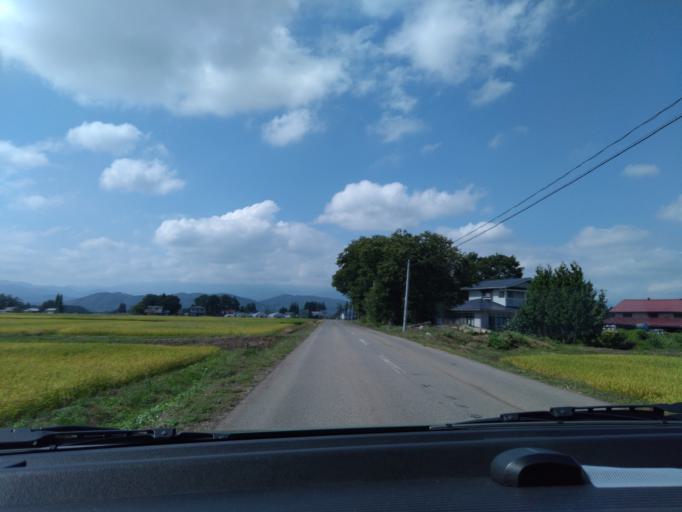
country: JP
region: Iwate
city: Shizukuishi
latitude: 39.6740
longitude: 140.9655
